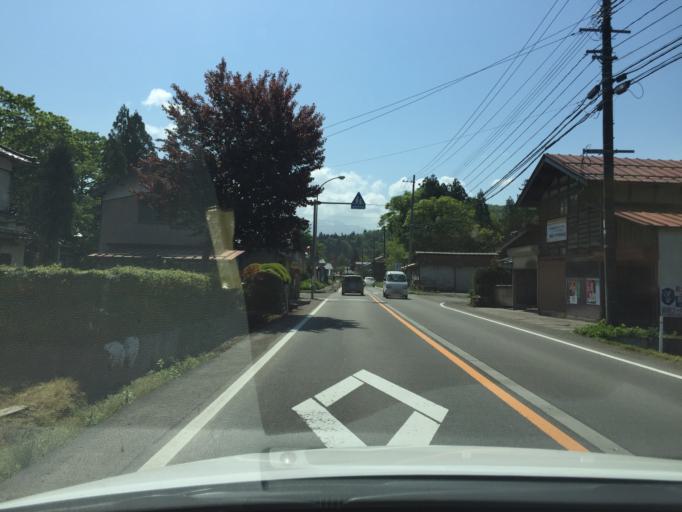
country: JP
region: Niigata
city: Kamo
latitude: 37.6296
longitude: 139.0960
